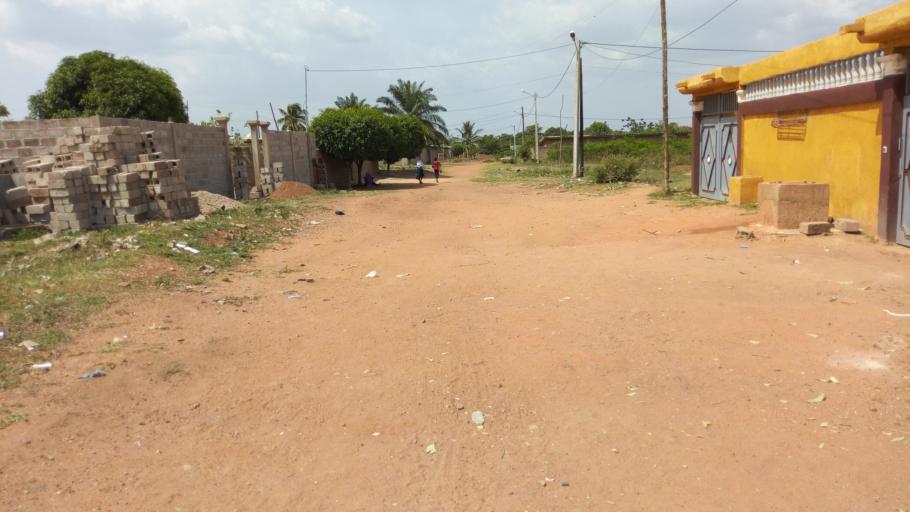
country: CI
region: Vallee du Bandama
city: Bouake
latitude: 7.7085
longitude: -5.0452
